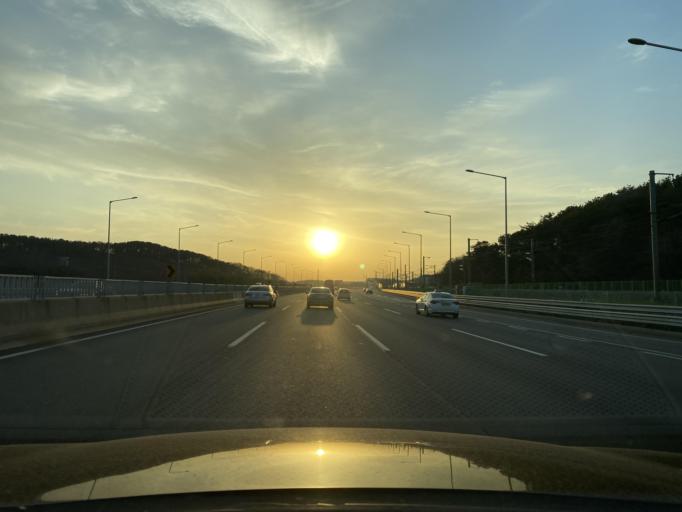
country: KR
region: Incheon
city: Incheon
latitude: 37.5152
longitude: 126.5330
